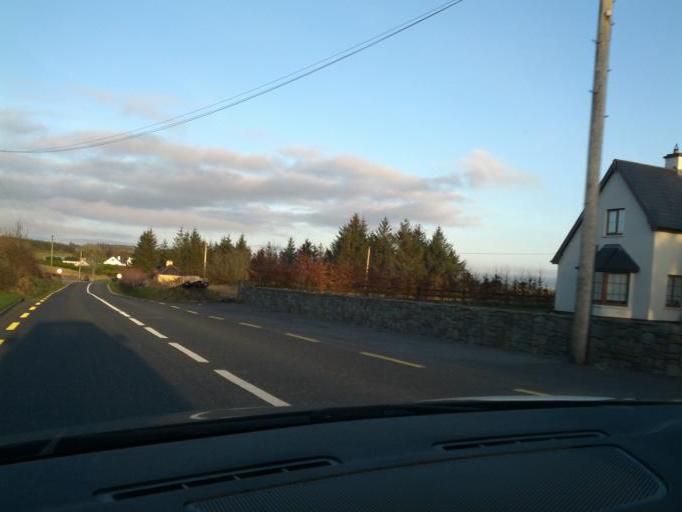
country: IE
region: Connaught
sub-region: Sligo
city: Tobercurry
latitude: 54.0515
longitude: -8.7098
